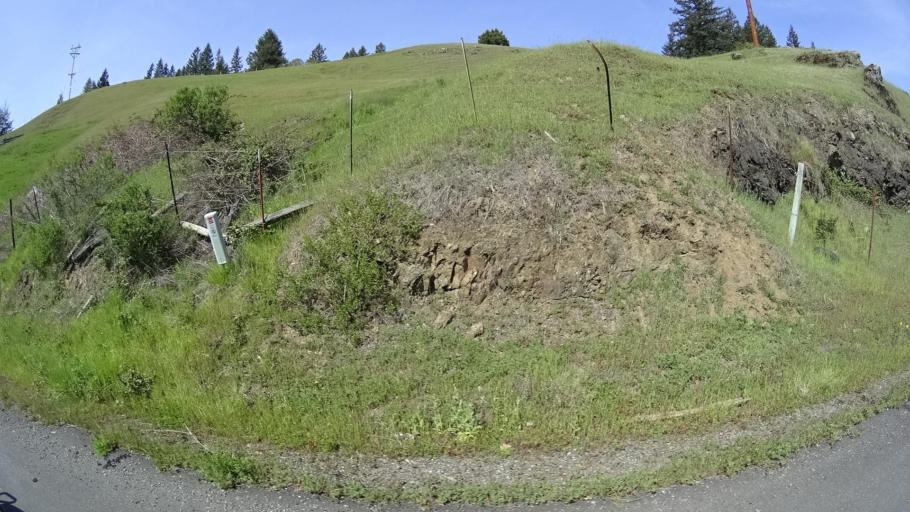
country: US
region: California
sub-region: Humboldt County
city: Redway
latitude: 40.4136
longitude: -123.7585
